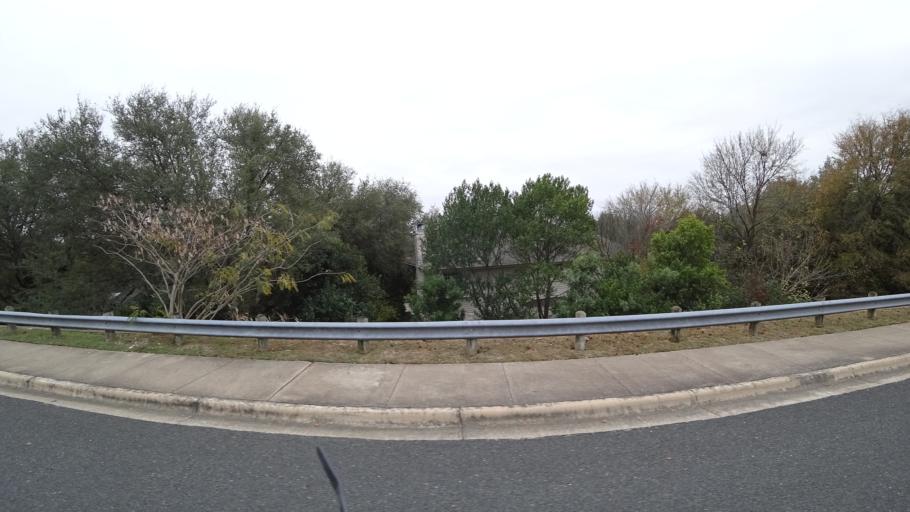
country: US
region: Texas
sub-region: Williamson County
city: Jollyville
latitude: 30.3792
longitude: -97.7881
